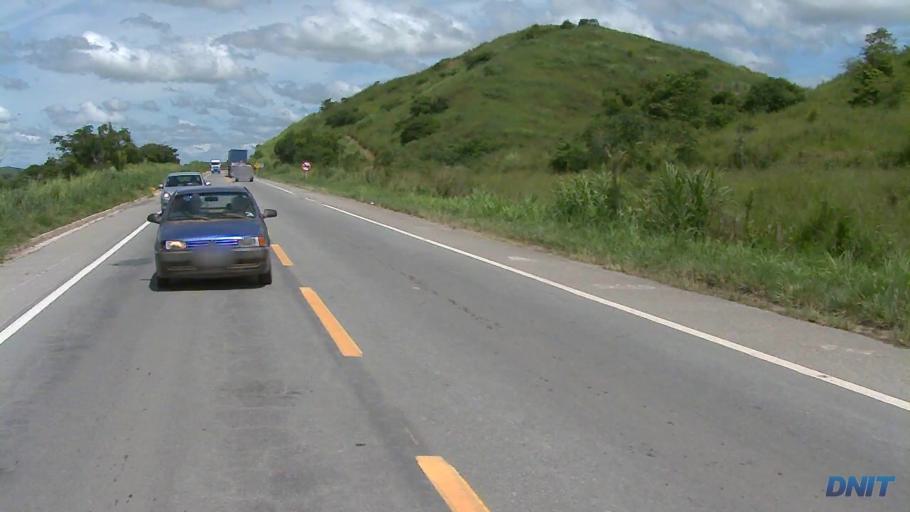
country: BR
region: Minas Gerais
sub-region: Governador Valadares
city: Governador Valadares
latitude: -18.9655
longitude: -42.0824
